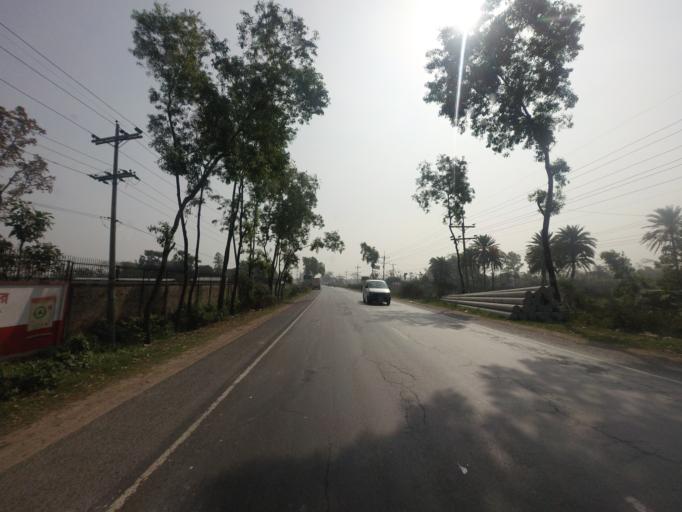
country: BD
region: Dhaka
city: Narsingdi
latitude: 23.8552
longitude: 90.6505
